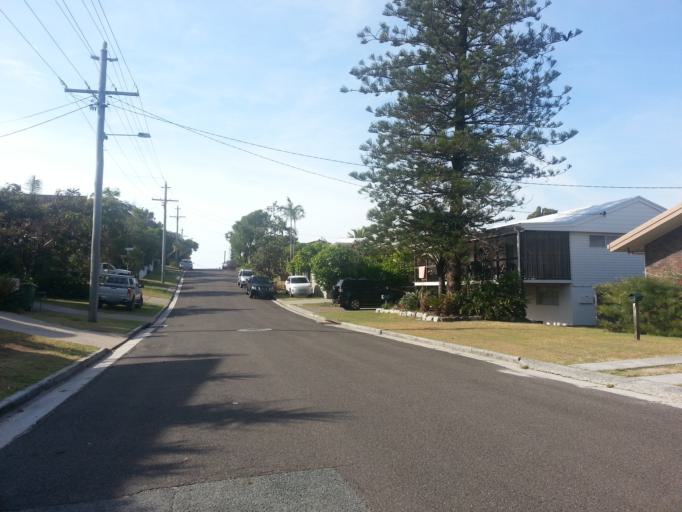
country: AU
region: Queensland
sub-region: Sunshine Coast
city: Peregian Springs
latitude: -26.4932
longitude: 153.0937
